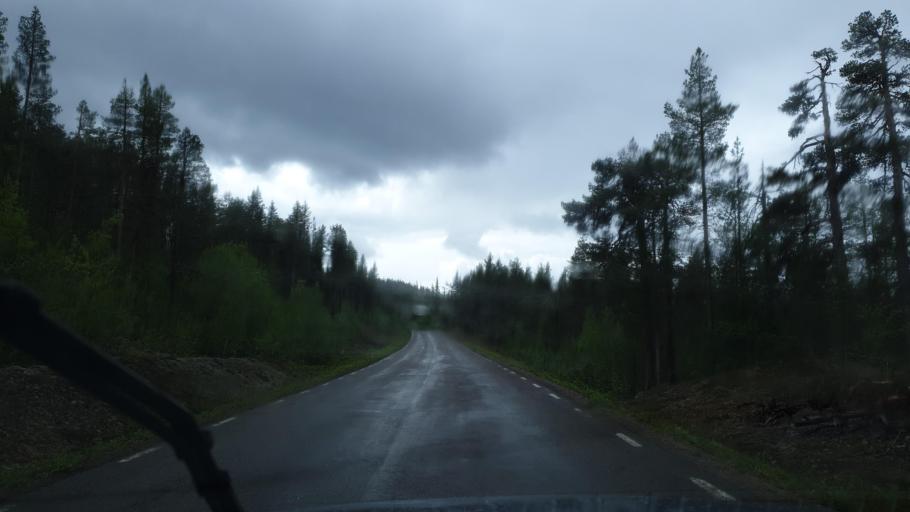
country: SE
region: Norrbotten
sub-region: Gallivare Kommun
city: Malmberget
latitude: 67.8924
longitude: 21.0465
